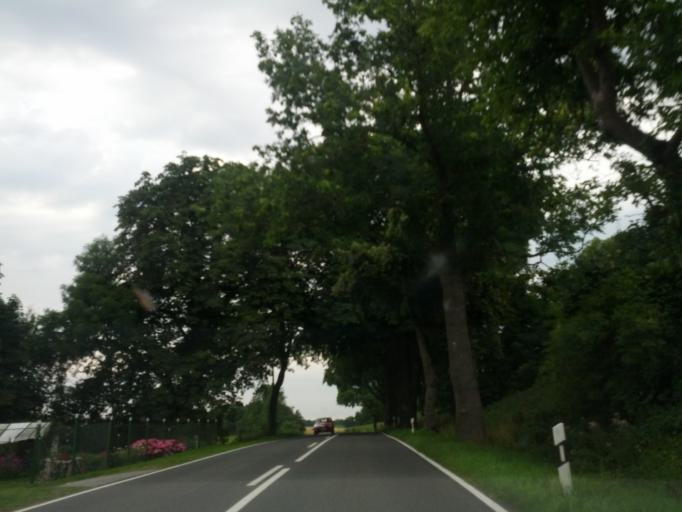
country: DE
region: Mecklenburg-Vorpommern
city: Satow-Oberhagen
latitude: 53.9971
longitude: 11.8424
